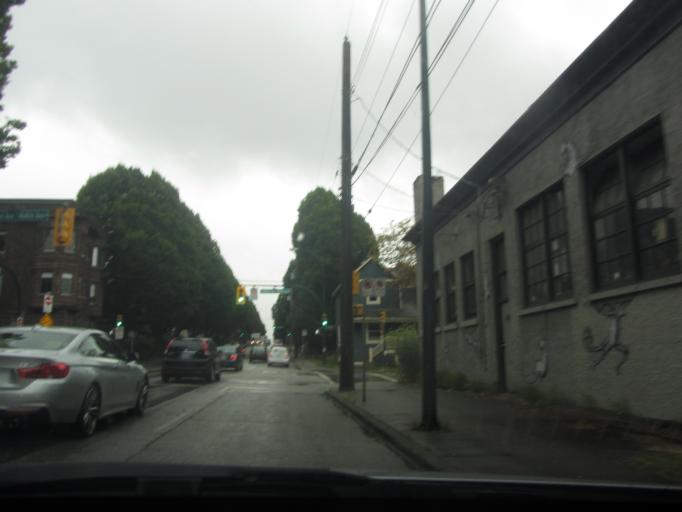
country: CA
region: British Columbia
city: Vancouver
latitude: 49.2766
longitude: -123.0940
